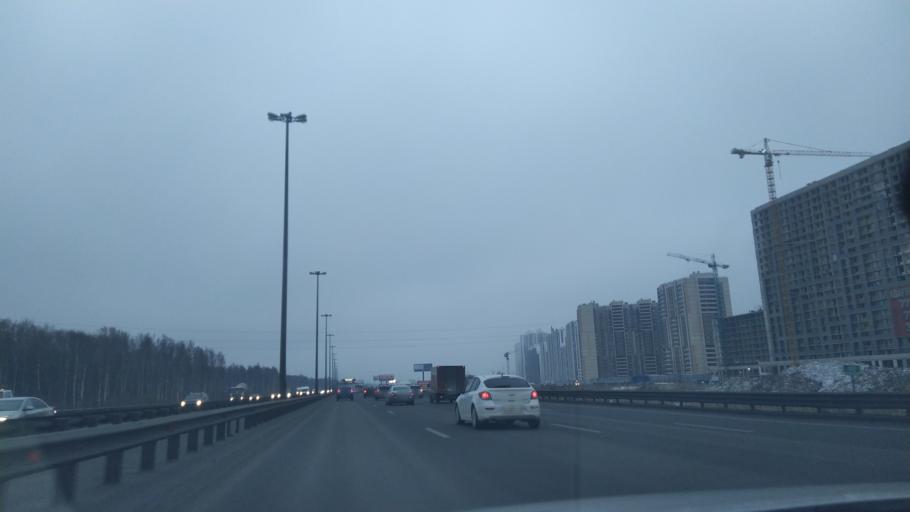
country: RU
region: Leningrad
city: Rybatskoye
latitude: 59.9117
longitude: 30.5259
